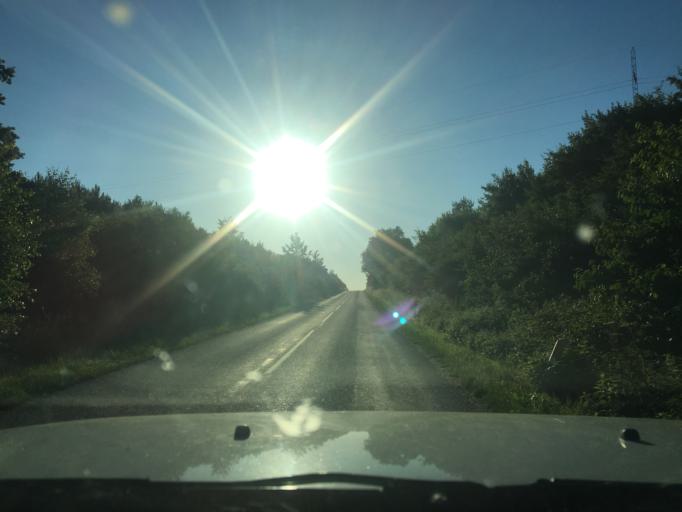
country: DK
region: Central Jutland
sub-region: Randers Kommune
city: Langa
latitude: 56.3923
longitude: 9.8739
